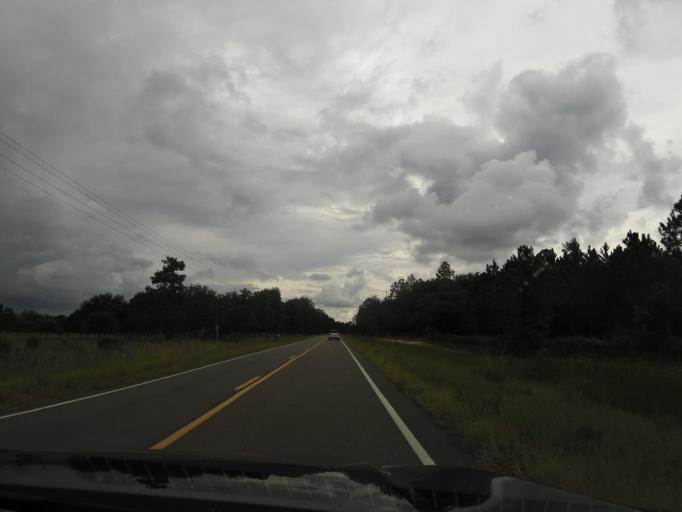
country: US
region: Florida
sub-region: Baker County
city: Macclenny
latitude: 30.4096
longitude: -82.1907
